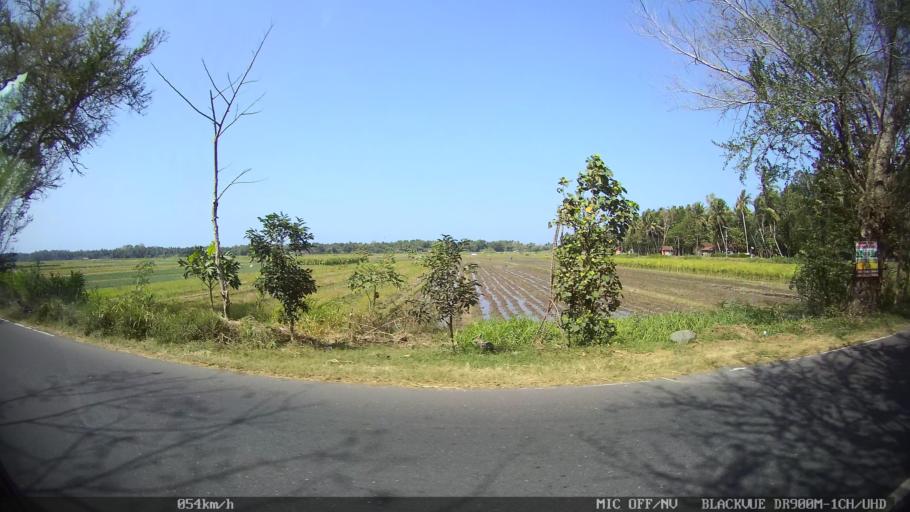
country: ID
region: Daerah Istimewa Yogyakarta
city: Srandakan
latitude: -7.9322
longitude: 110.2131
